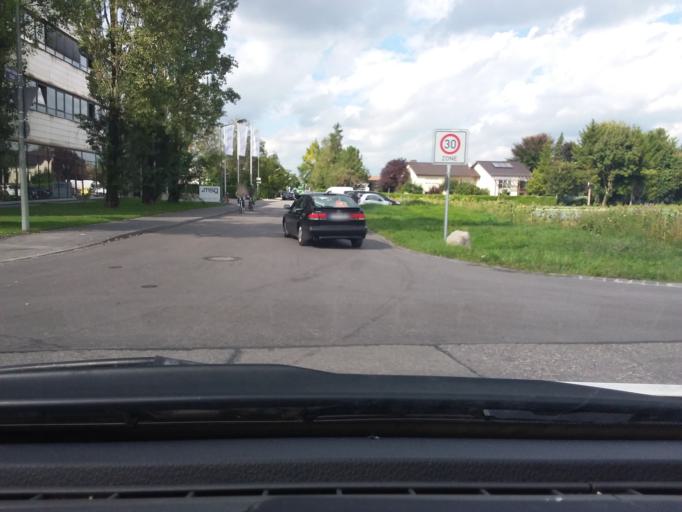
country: DE
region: Bavaria
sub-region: Upper Bavaria
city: Ismaning
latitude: 48.2283
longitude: 11.6865
